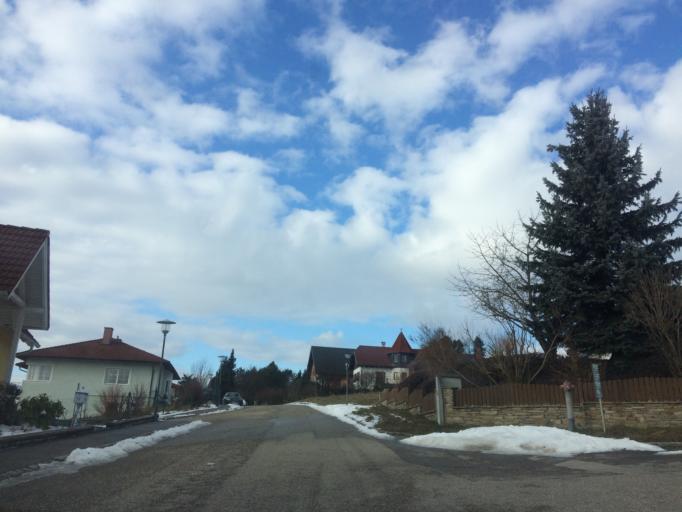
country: AT
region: Lower Austria
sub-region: Politischer Bezirk Wien-Umgebung
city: Gablitz
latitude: 48.2302
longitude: 16.1553
